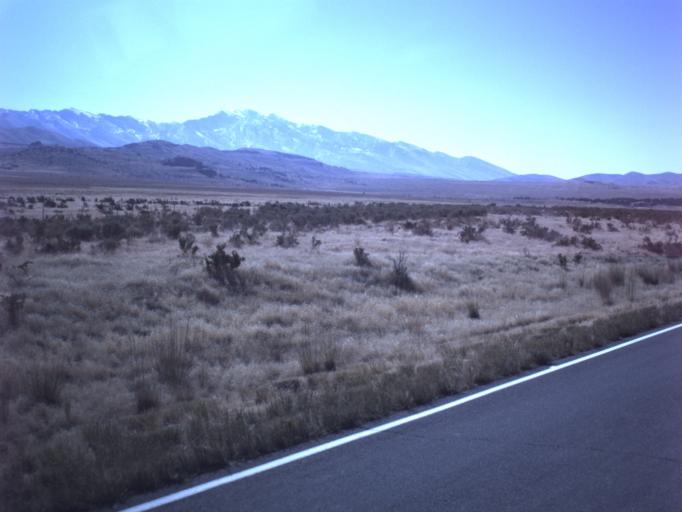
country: US
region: Utah
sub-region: Tooele County
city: Grantsville
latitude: 40.6297
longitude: -112.6957
